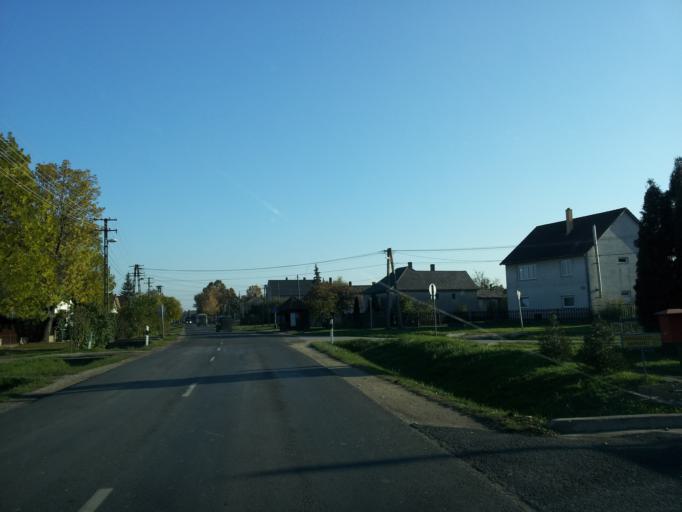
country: HU
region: Fejer
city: Fehervarcsurgo
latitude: 47.2955
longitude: 18.2623
